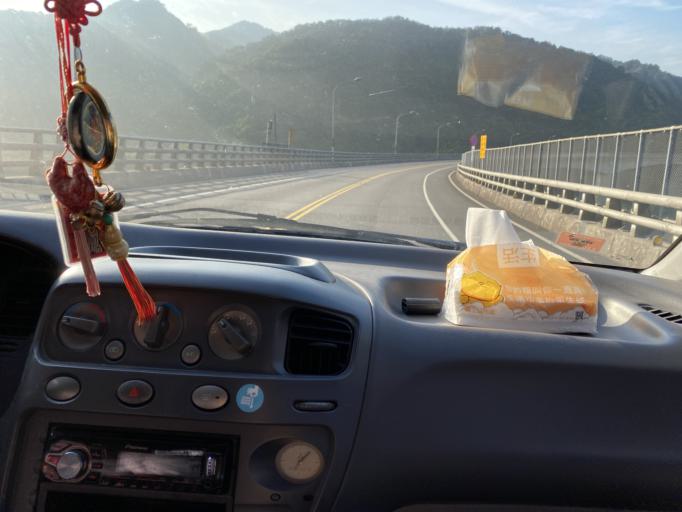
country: TW
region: Taiwan
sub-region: Keelung
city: Keelung
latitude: 25.0458
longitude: 121.7797
